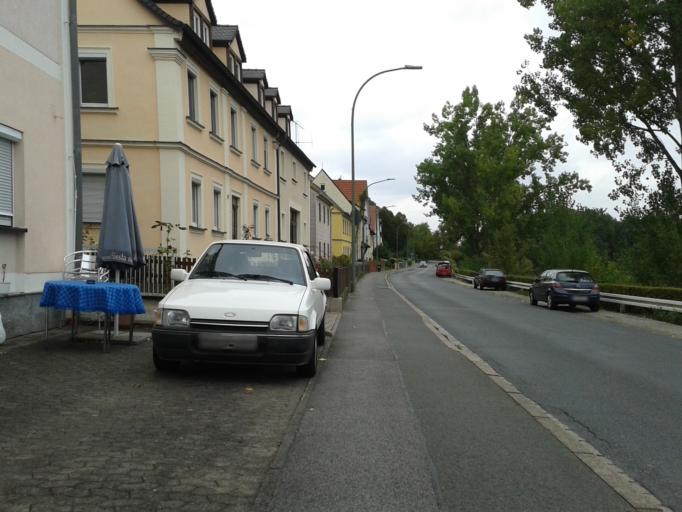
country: DE
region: Bavaria
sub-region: Upper Franconia
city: Bamberg
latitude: 49.8693
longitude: 10.9054
